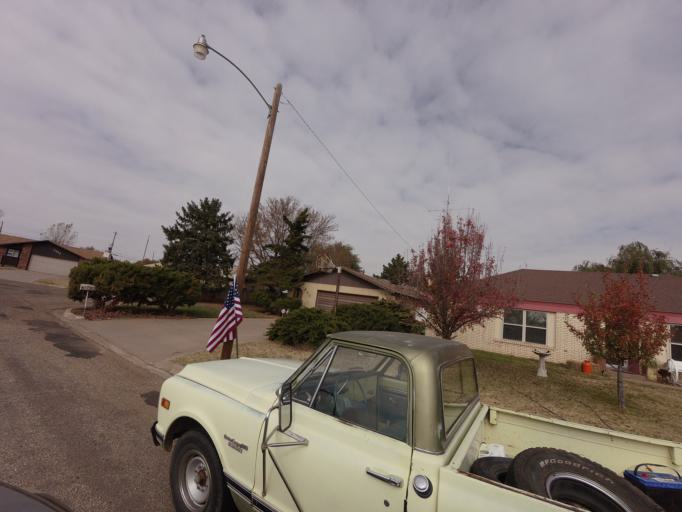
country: US
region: New Mexico
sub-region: Curry County
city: Clovis
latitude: 34.4313
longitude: -103.2169
